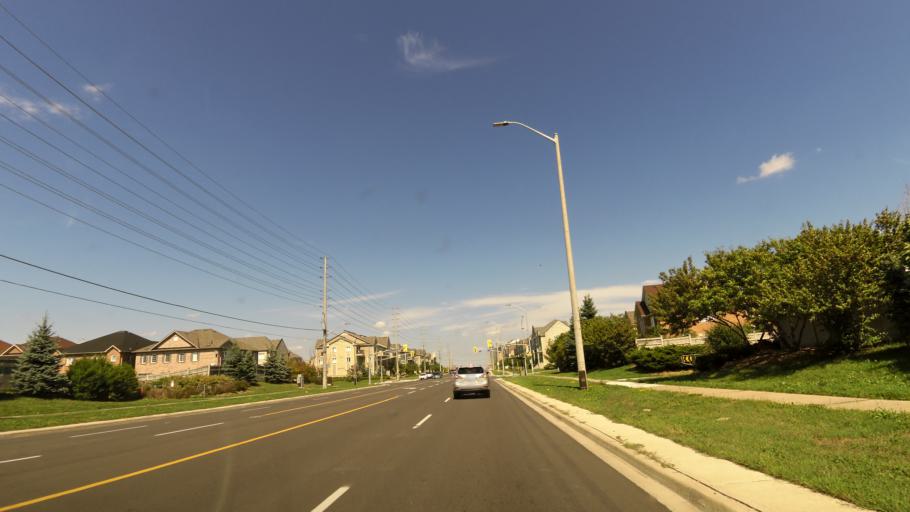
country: CA
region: Ontario
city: Mississauga
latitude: 43.5460
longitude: -79.7210
